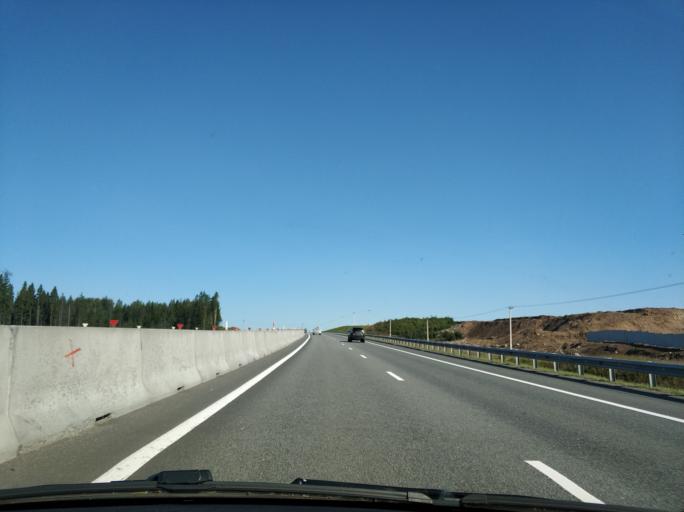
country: RU
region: Leningrad
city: Sosnovo
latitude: 60.5106
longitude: 30.1890
